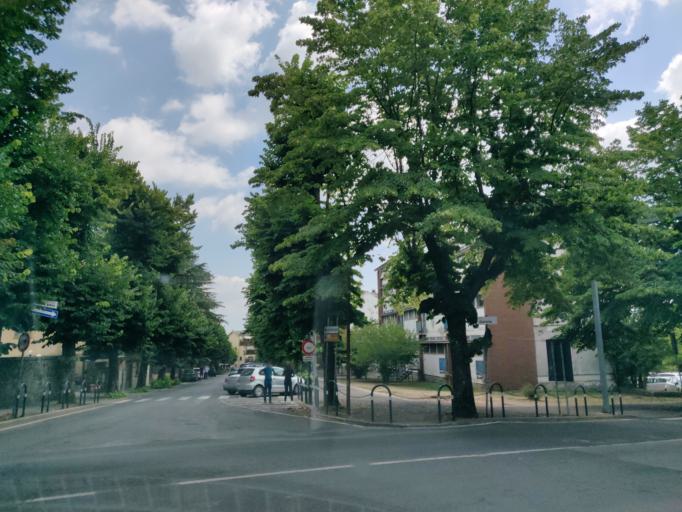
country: IT
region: Tuscany
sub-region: Provincia di Siena
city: Abbadia San Salvatore
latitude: 42.8810
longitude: 11.6742
